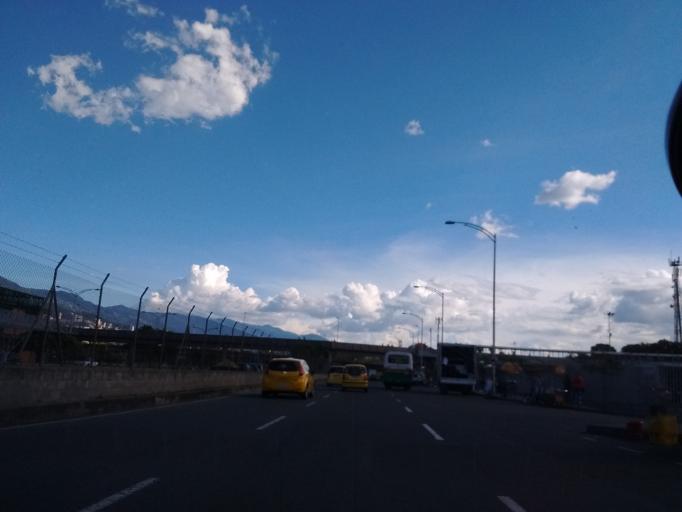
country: CO
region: Antioquia
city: Medellin
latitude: 6.2786
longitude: -75.5700
